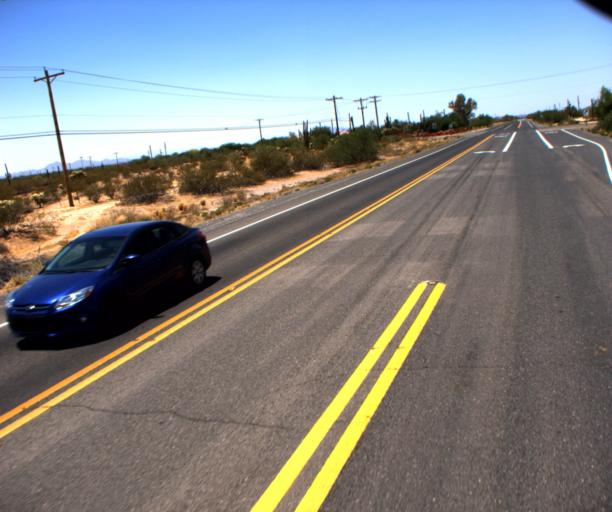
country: US
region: Arizona
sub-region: Pinal County
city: Florence
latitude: 32.9574
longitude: -111.3324
